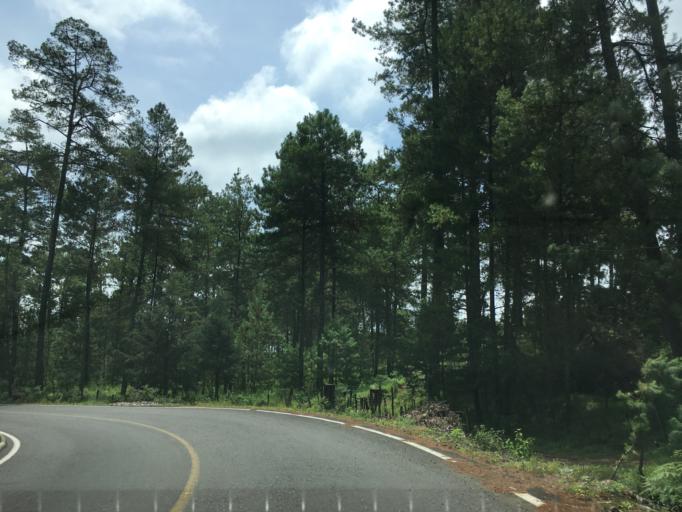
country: MX
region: Michoacan
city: Nuevo San Juan Parangaricutiro
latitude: 19.4432
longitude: -102.1691
